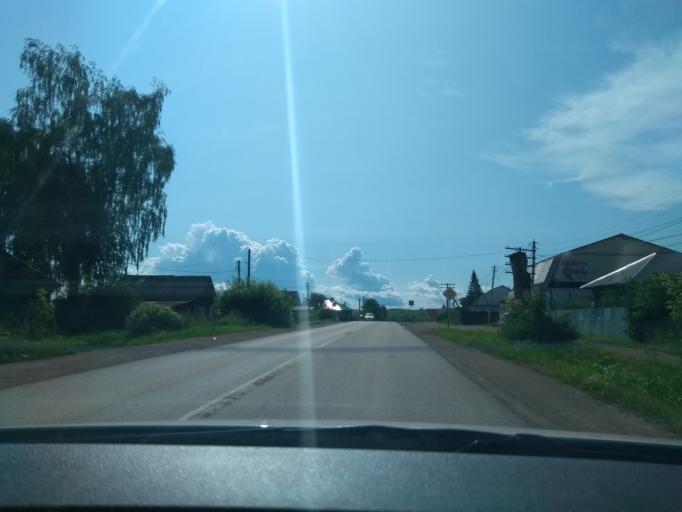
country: RU
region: Perm
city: Lobanovo
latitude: 57.8602
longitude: 56.3027
